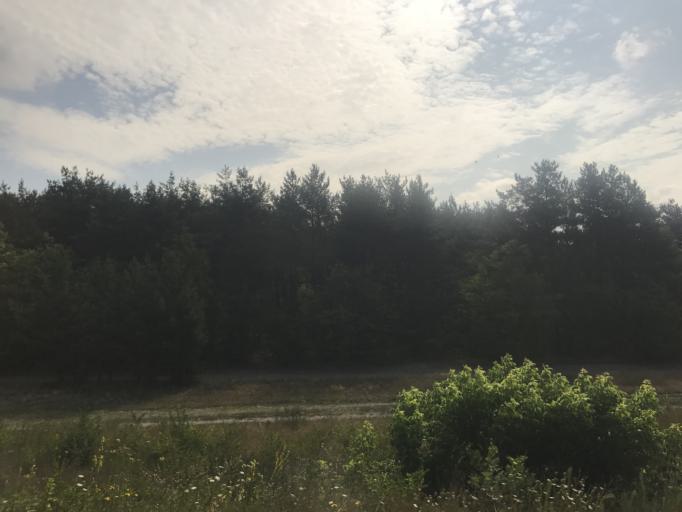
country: PL
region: Kujawsko-Pomorskie
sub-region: Bydgoszcz
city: Bydgoszcz
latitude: 53.1461
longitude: 18.0055
